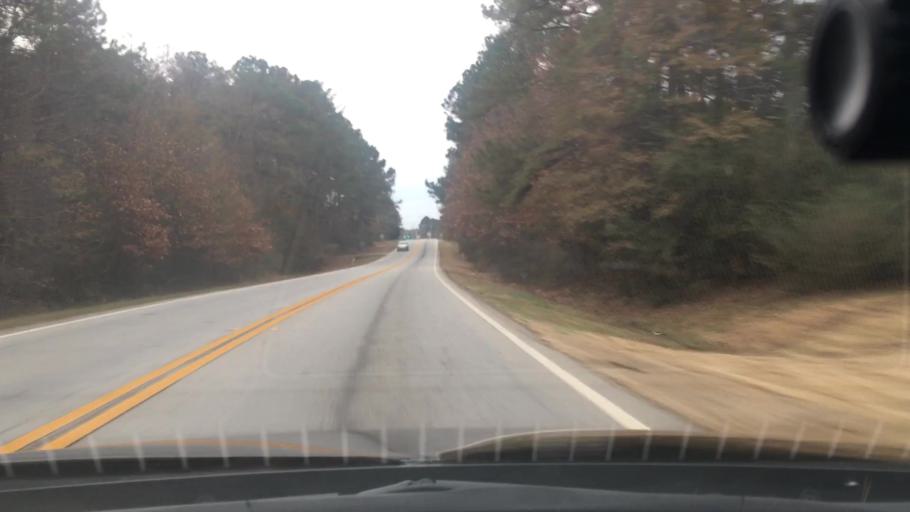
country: US
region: Georgia
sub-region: Fayette County
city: Peachtree City
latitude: 33.3653
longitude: -84.6304
